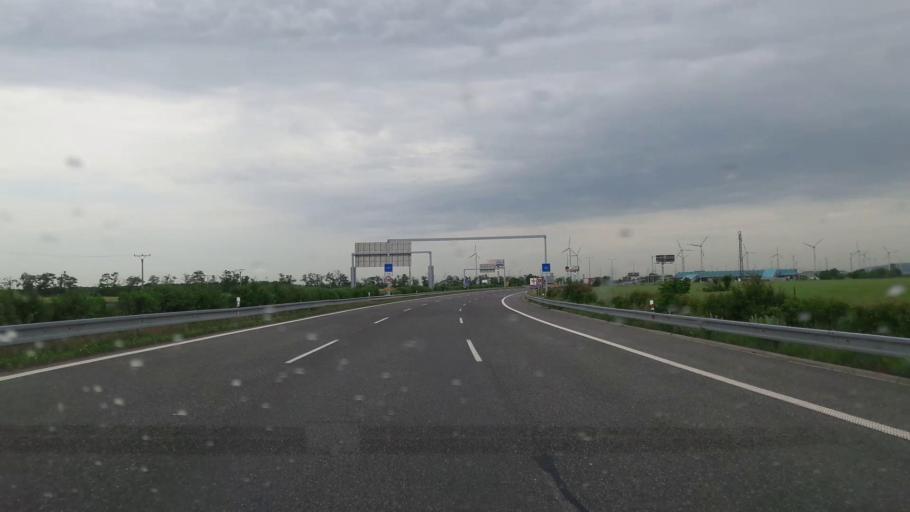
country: AT
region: Burgenland
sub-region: Politischer Bezirk Neusiedl am See
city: Kittsee
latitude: 48.0701
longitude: 17.0870
